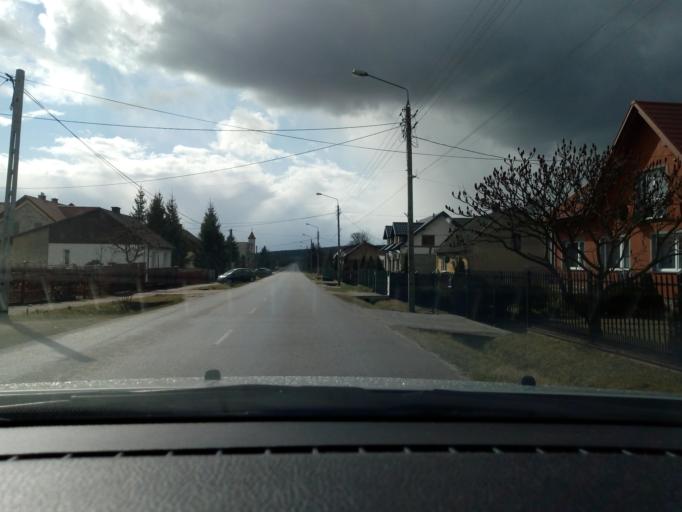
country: PL
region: Swietokrzyskie
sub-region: Powiat skarzyski
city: Skarzysko Koscielne
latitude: 51.1521
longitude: 20.8941
